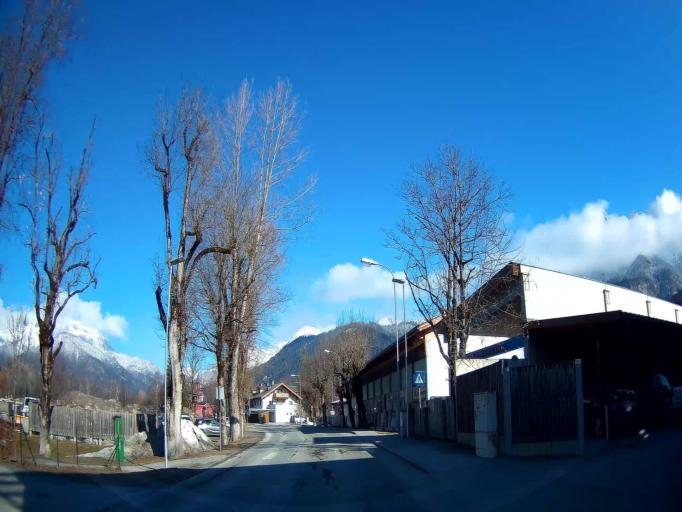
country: AT
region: Salzburg
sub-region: Politischer Bezirk Zell am See
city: Saalfelden am Steinernen Meer
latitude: 47.4307
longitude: 12.8523
